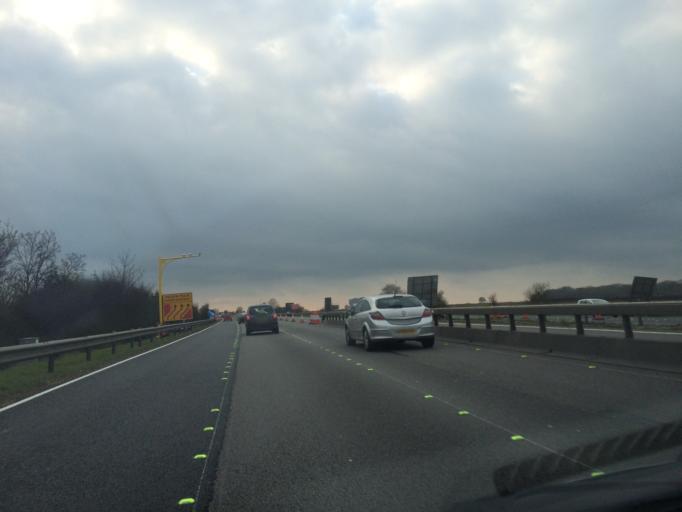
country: GB
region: England
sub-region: West Berkshire
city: Winterbourne
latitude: 51.4562
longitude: -1.3497
